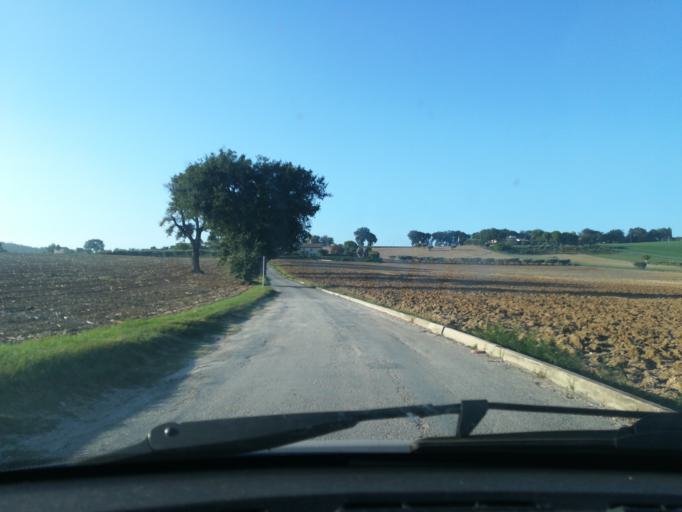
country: IT
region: The Marches
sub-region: Provincia di Macerata
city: Piediripa
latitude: 43.2750
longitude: 13.4659
